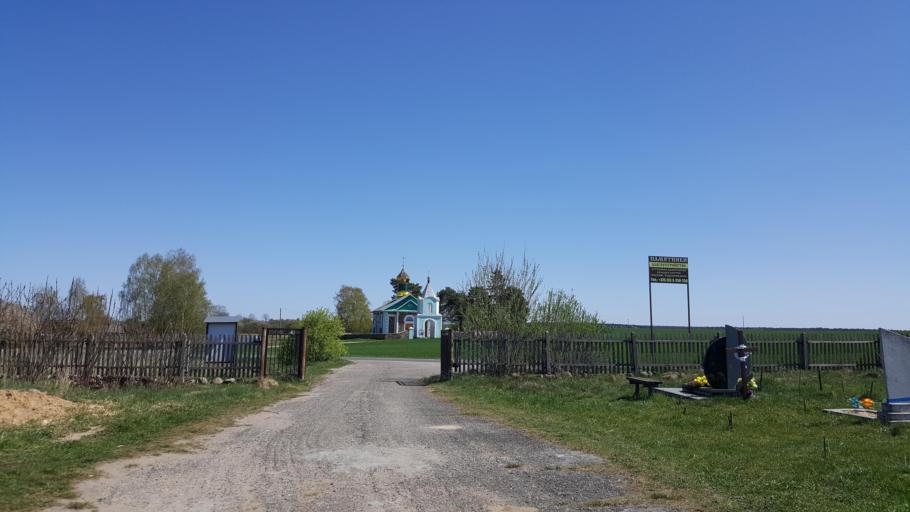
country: BY
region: Brest
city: Vysokaye
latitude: 52.3566
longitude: 23.5068
